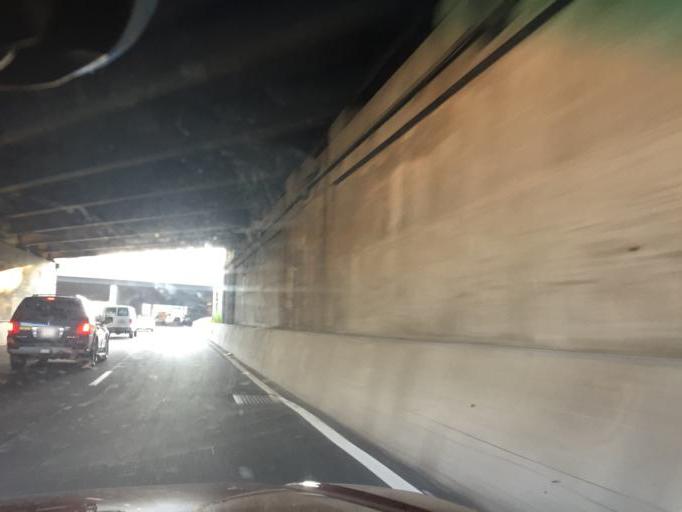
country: US
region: New York
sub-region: Queens County
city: Long Island City
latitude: 40.7398
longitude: -73.9000
